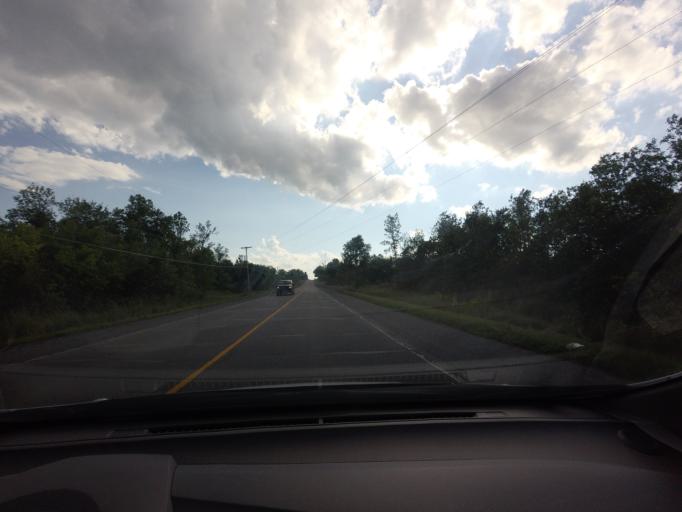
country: CA
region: Ontario
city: Carleton Place
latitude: 45.0991
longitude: -75.9794
